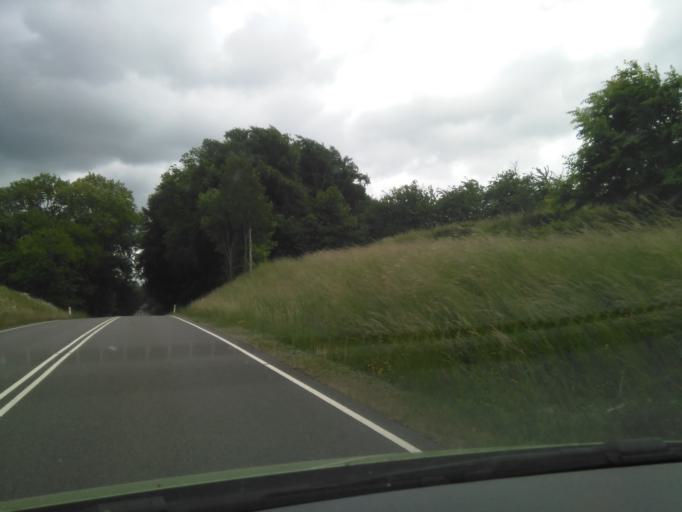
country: DK
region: Capital Region
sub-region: Bornholm Kommune
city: Akirkeby
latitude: 55.2295
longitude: 14.8795
